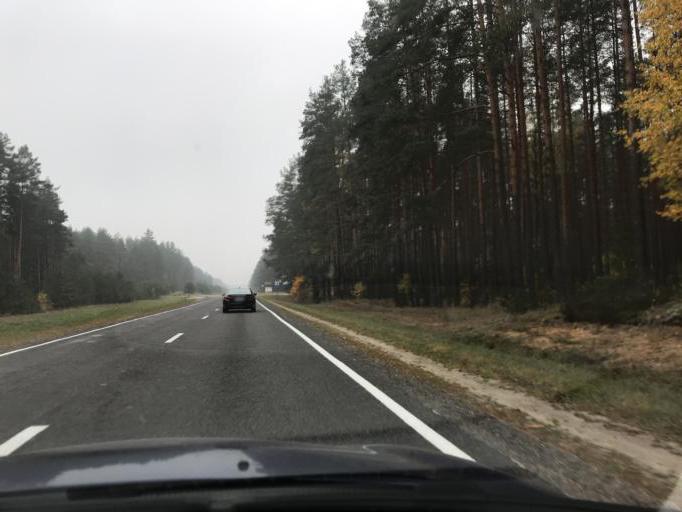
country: LT
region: Alytaus apskritis
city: Druskininkai
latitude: 53.8642
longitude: 23.8934
